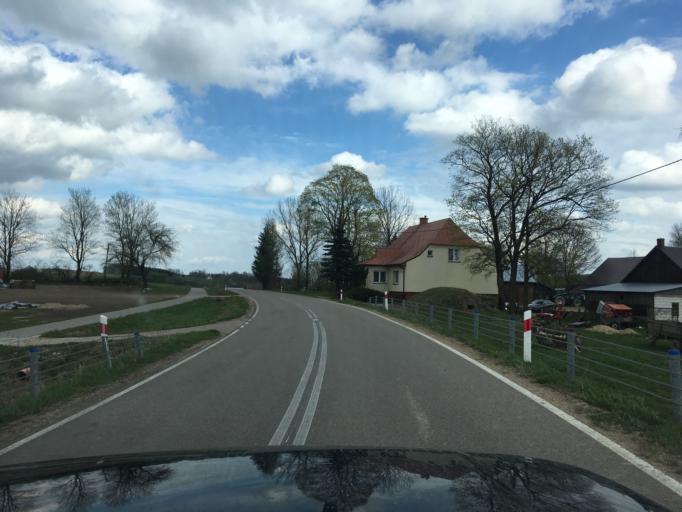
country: PL
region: Podlasie
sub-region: Powiat suwalski
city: Filipow
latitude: 54.3614
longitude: 22.7979
